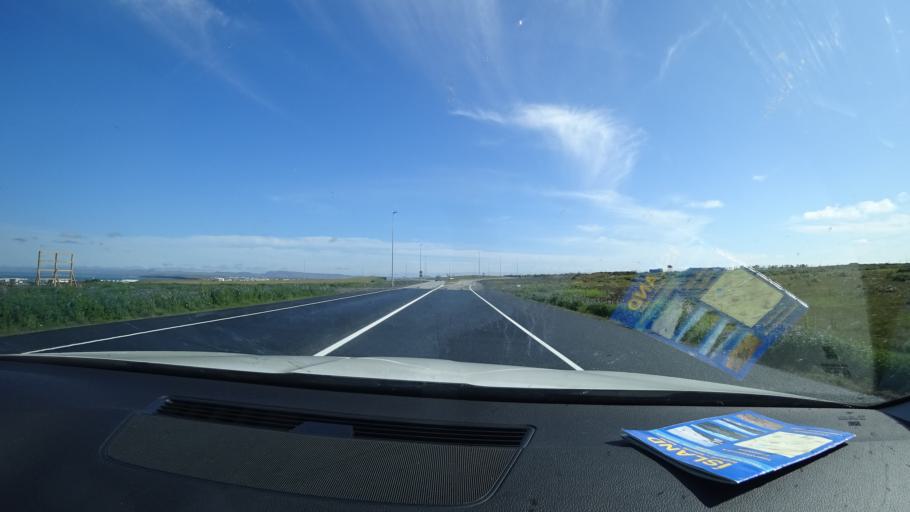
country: IS
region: Southern Peninsula
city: Reykjanesbaer
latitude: 63.9919
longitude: -22.5802
